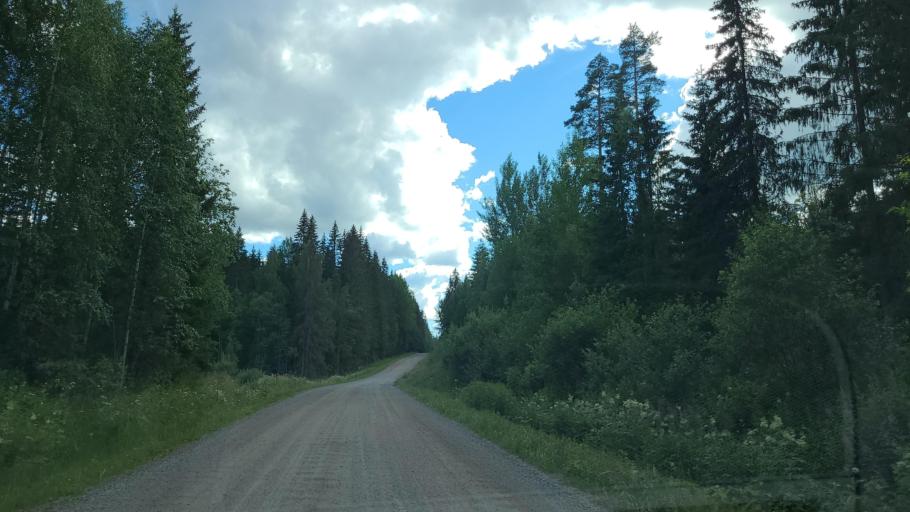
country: FI
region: Central Finland
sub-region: Jaemsae
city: Jaemsae
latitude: 61.9218
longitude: 25.3113
